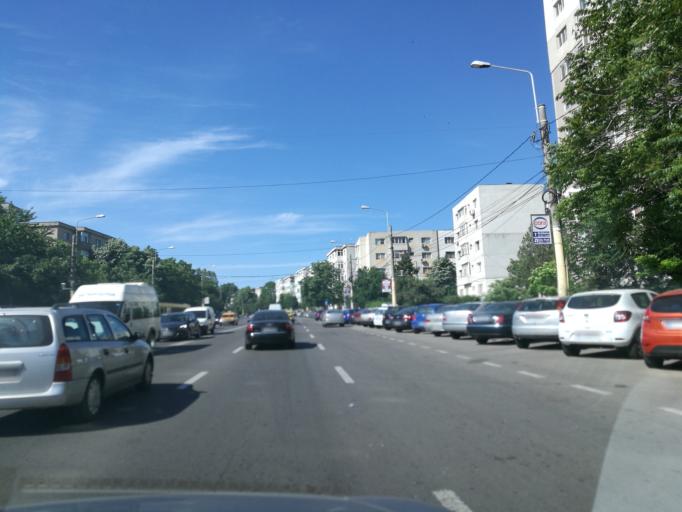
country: RO
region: Constanta
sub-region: Municipiul Constanta
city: Constanta
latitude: 44.2001
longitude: 28.6262
